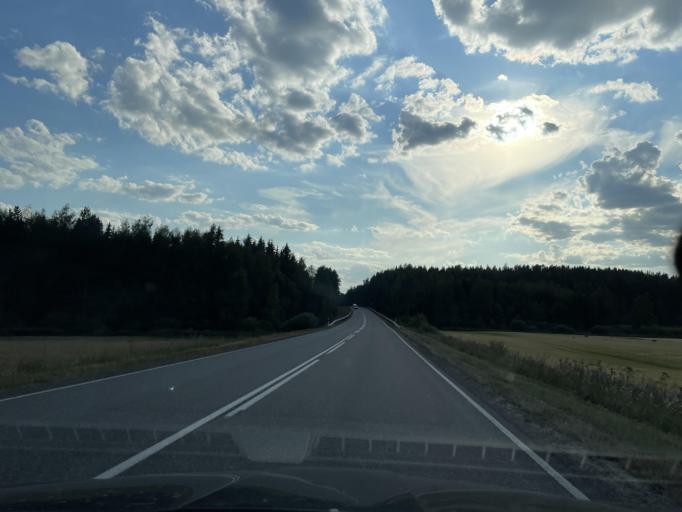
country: FI
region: Haeme
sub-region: Haemeenlinna
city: Lammi
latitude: 61.1317
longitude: 24.9803
